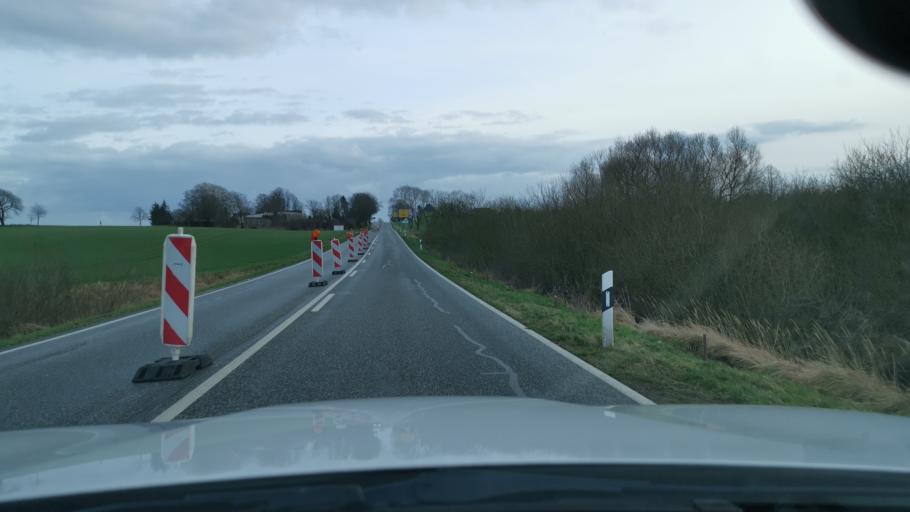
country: DE
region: Mecklenburg-Vorpommern
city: Dummerstorf
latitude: 53.9760
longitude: 12.2828
